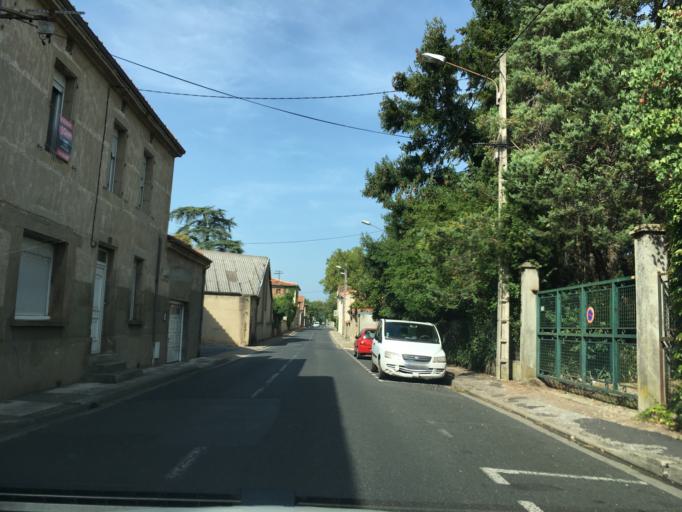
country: FR
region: Midi-Pyrenees
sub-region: Departement du Tarn
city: Castres
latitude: 43.6104
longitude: 2.2468
